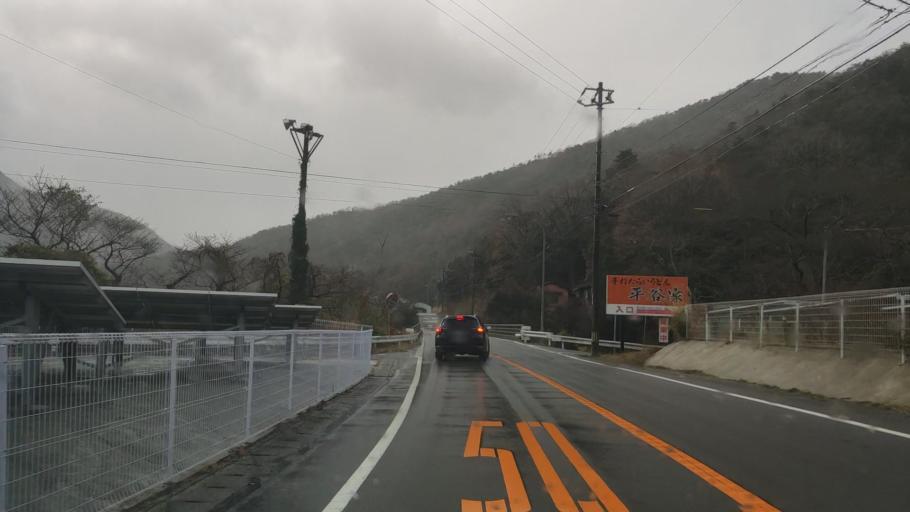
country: JP
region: Tokushima
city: Kamojimacho-jogejima
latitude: 34.1530
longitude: 134.3530
